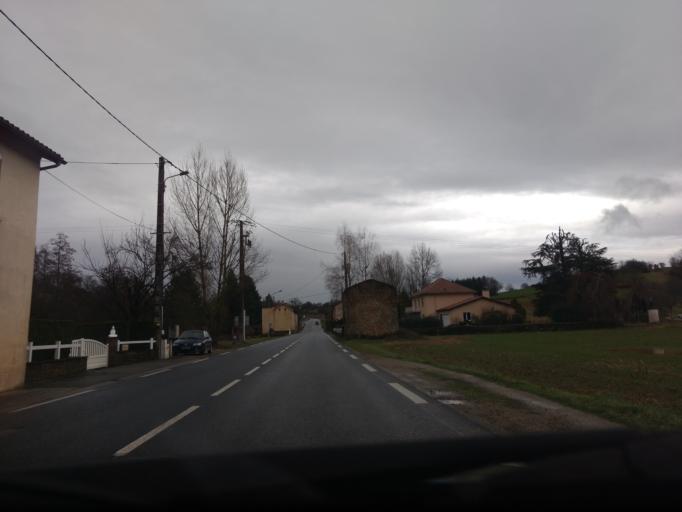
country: FR
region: Midi-Pyrenees
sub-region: Departement de l'Aveyron
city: Firmi
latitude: 44.5249
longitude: 2.3327
